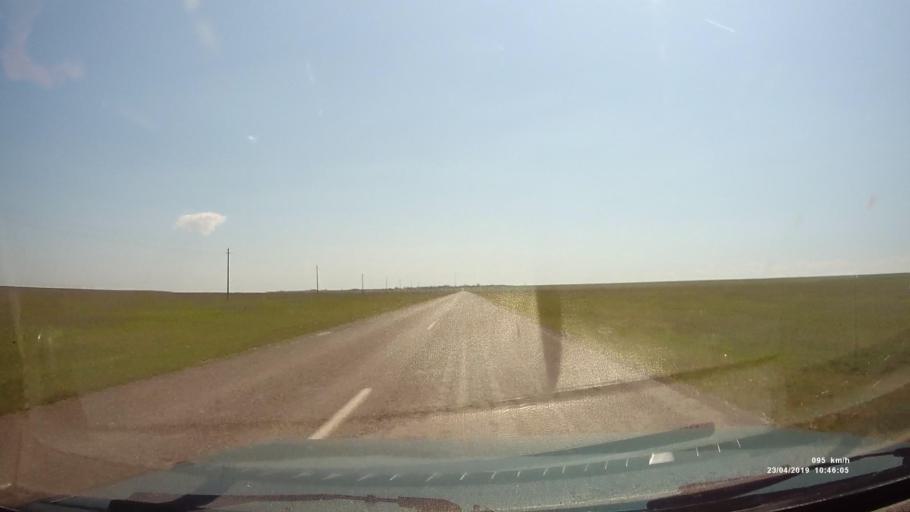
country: RU
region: Kalmykiya
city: Yashalta
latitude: 46.4459
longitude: 42.6854
